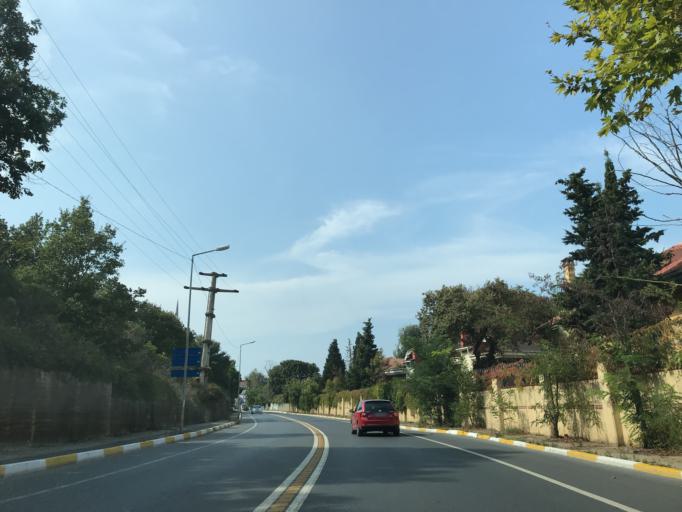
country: TR
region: Istanbul
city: Arikoey
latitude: 41.2437
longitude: 29.0401
